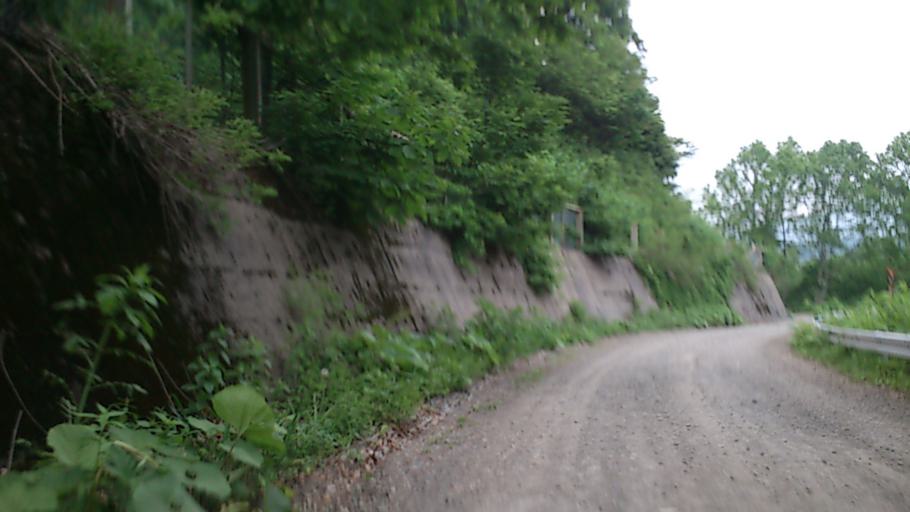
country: JP
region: Aomori
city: Hirosaki
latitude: 40.5572
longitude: 140.1647
